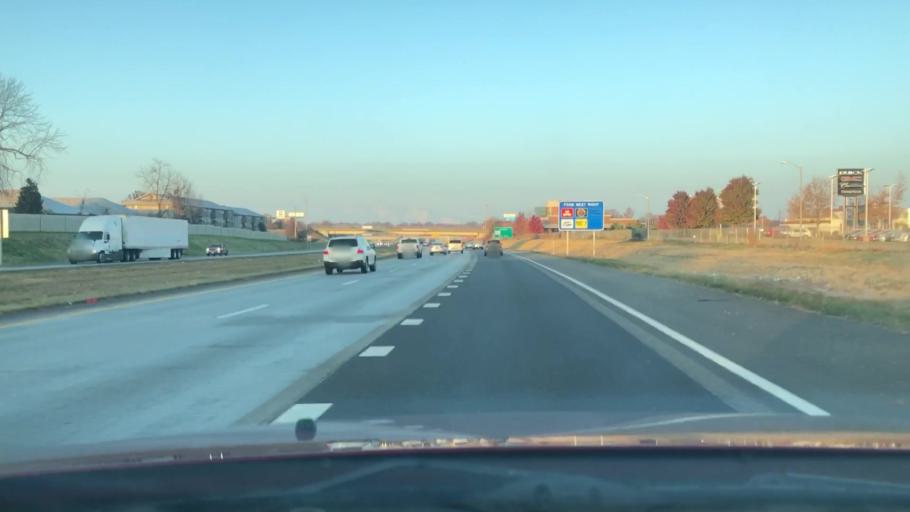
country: US
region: Missouri
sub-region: Greene County
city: Springfield
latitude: 37.1422
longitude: -93.2678
